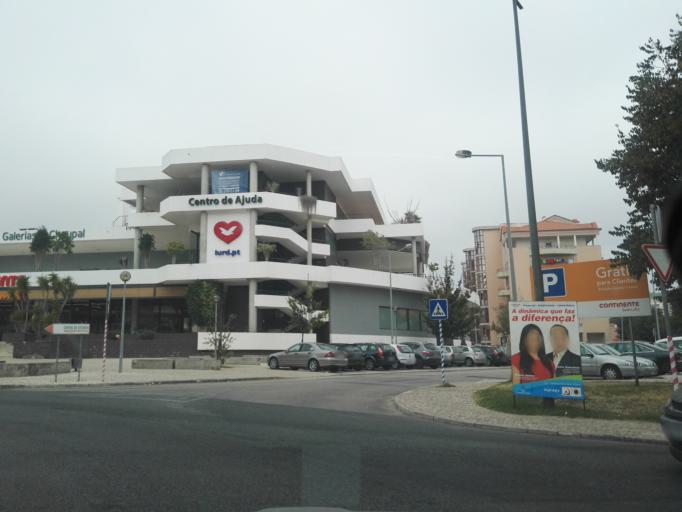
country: PT
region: Lisbon
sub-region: Vila Franca de Xira
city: Sobralinho
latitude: 38.9022
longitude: -9.0397
